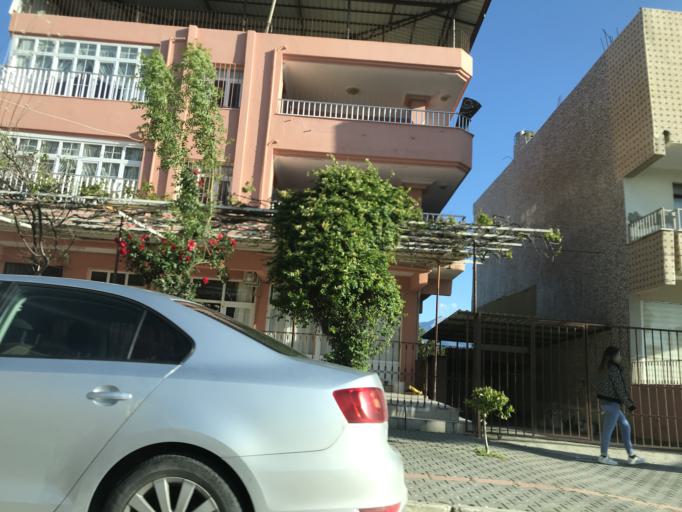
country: TR
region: Hatay
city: Samandag
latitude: 36.0831
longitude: 35.9556
